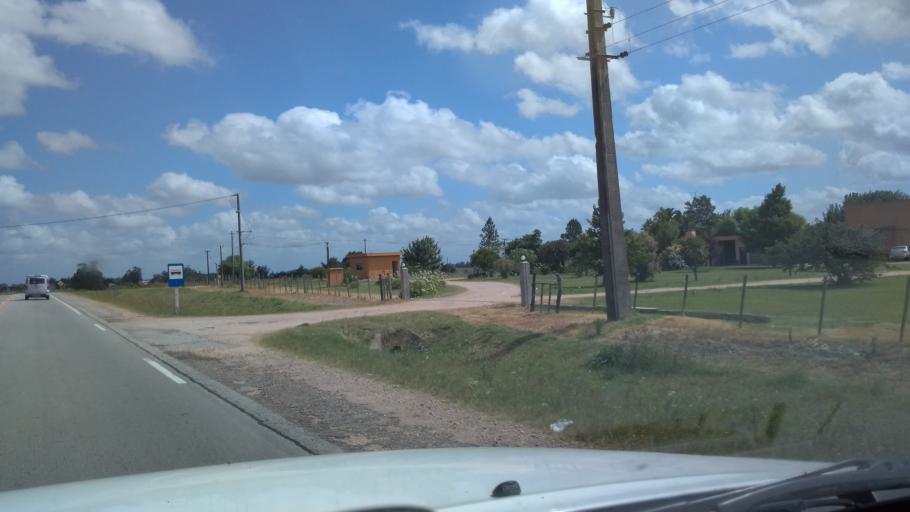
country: UY
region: Canelones
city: Santa Rosa
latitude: -34.5303
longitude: -56.0555
